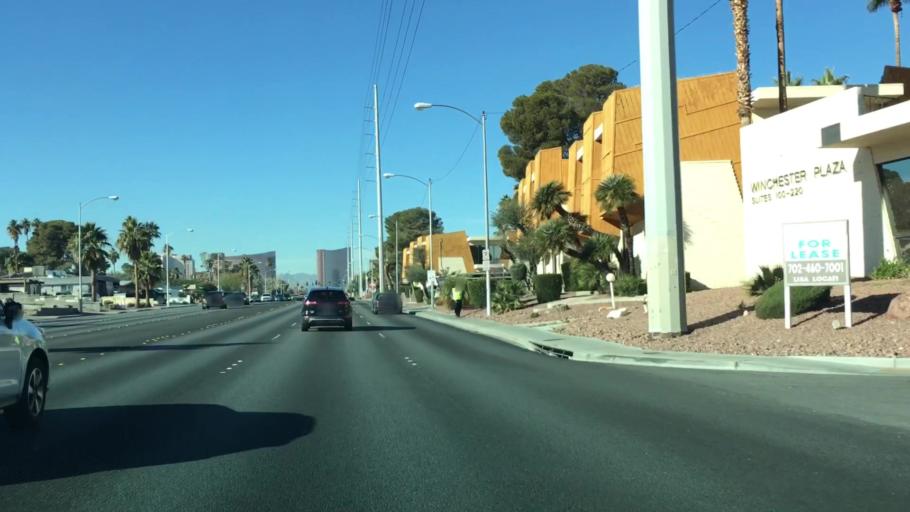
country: US
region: Nevada
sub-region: Clark County
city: Winchester
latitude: 36.1299
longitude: -115.1283
